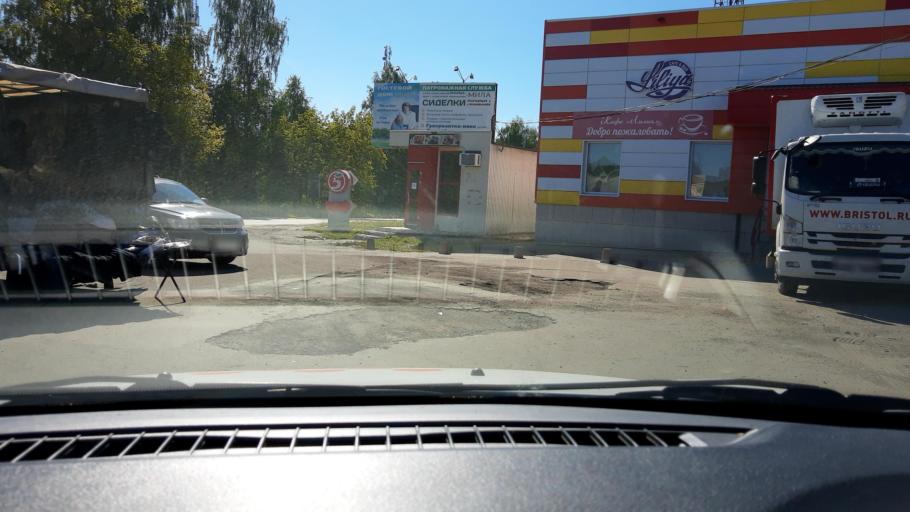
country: RU
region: Nizjnij Novgorod
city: Zavolzh'ye
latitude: 56.7159
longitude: 43.4142
